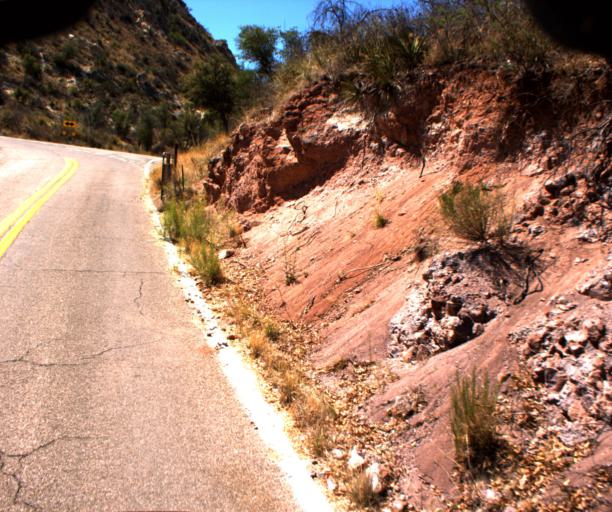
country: US
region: Arizona
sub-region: Santa Cruz County
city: Rio Rico
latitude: 31.3947
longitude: -111.0892
